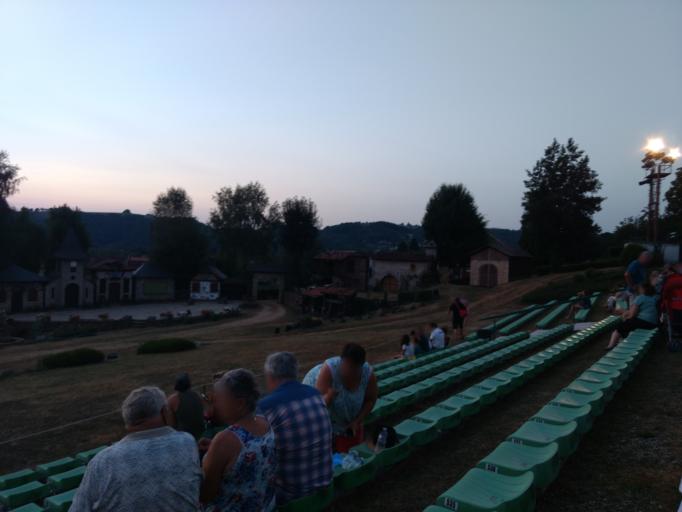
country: FR
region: Midi-Pyrenees
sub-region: Departement de l'Aveyron
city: Livinhac-le-Haut
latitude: 44.6046
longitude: 2.2499
